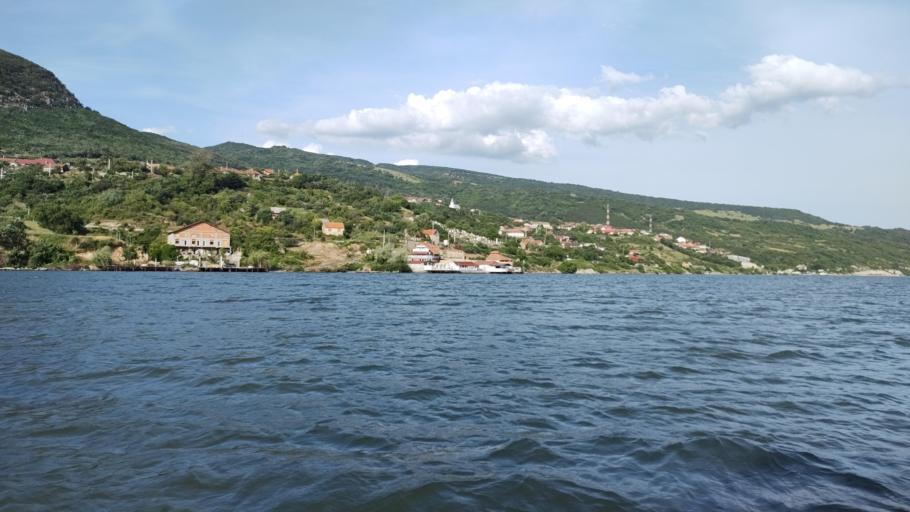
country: RO
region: Mehedinti
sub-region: Comuna Svinita
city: Svinita
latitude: 44.4981
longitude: 22.0921
